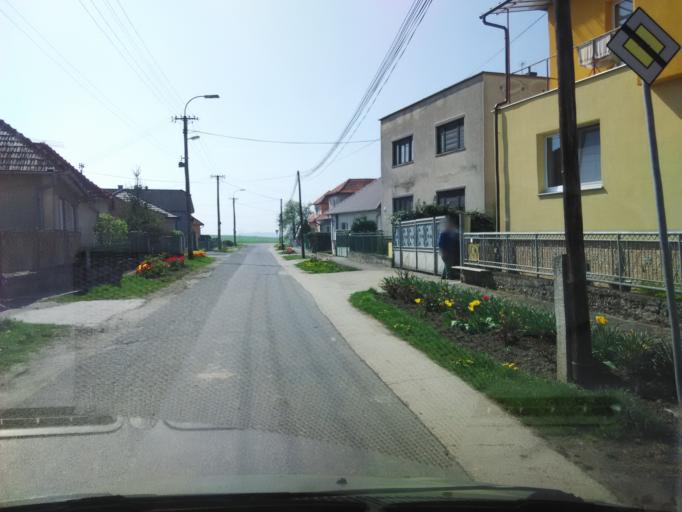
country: SK
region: Nitriansky
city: Tlmace
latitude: 48.2867
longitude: 18.6023
